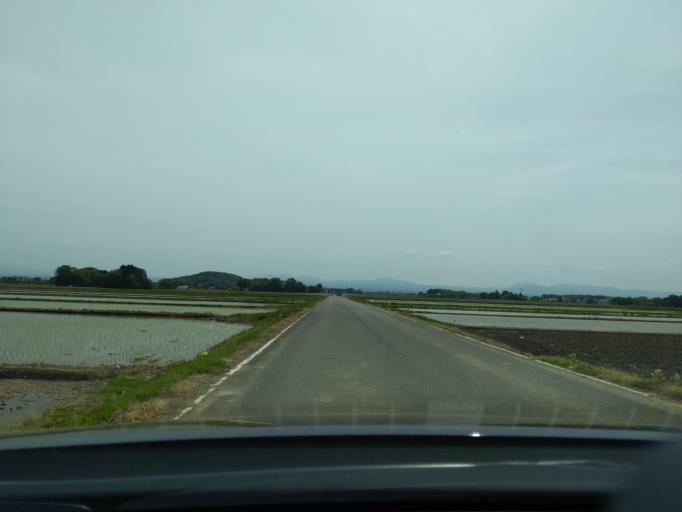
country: JP
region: Fukushima
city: Koriyama
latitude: 37.3985
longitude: 140.2783
